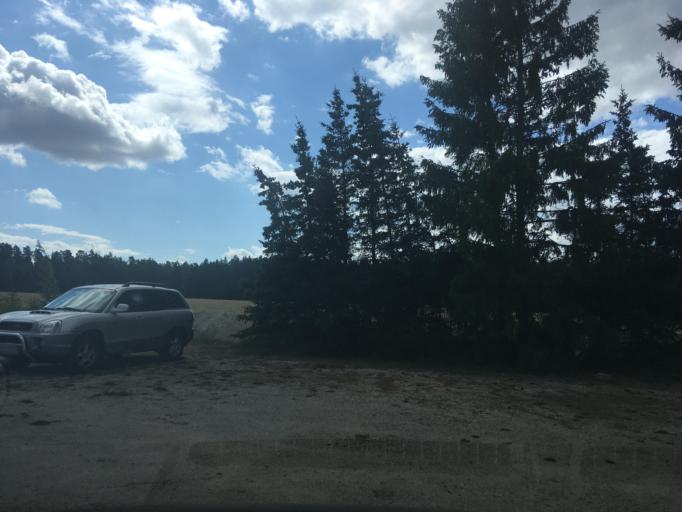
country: EE
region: Tartu
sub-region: Puhja vald
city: Puhja
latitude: 58.2235
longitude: 26.1313
